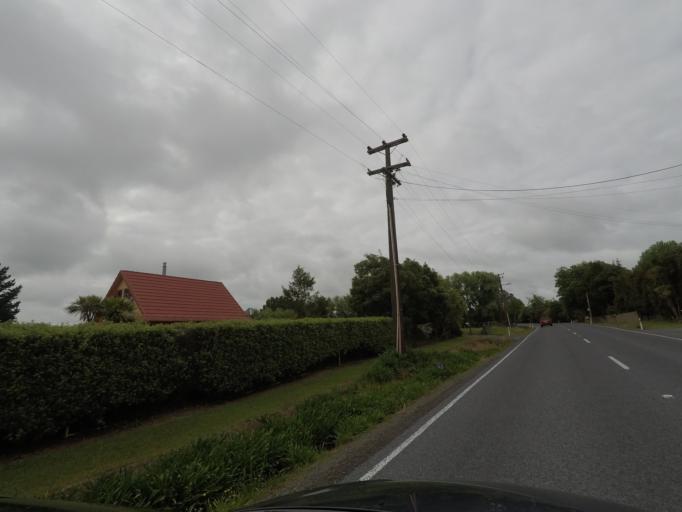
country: NZ
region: Auckland
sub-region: Auckland
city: Rosebank
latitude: -36.7916
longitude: 174.5746
